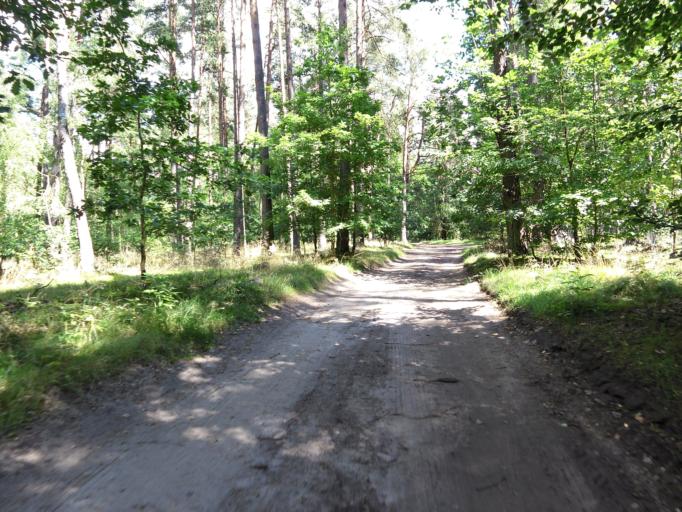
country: DE
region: Brandenburg
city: Lychen
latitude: 53.2752
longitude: 13.4326
